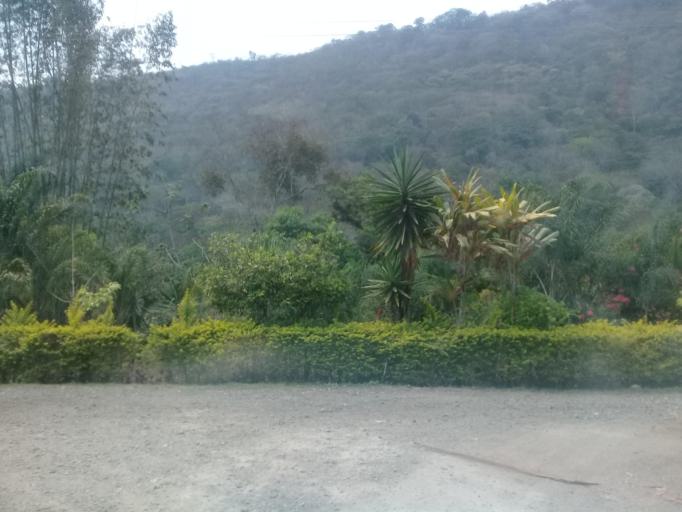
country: MX
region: Veracruz
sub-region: Cordoba
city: Fredepo
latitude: 18.8566
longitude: -96.9911
